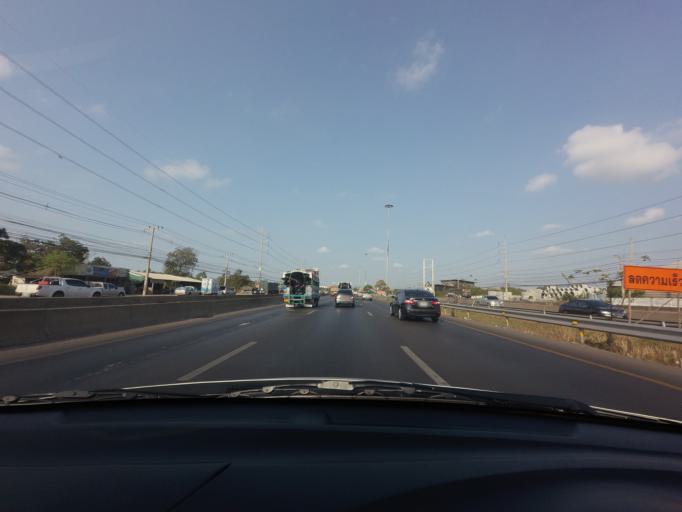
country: TH
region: Samut Sakhon
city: Samut Sakhon
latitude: 13.5386
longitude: 100.2270
